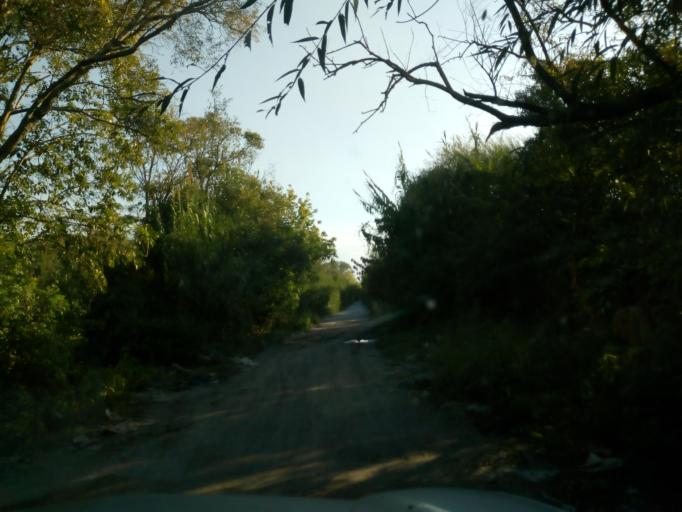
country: AR
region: Buenos Aires
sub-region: Partido de Ensenada
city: Ensenada
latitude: -34.7828
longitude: -58.0131
